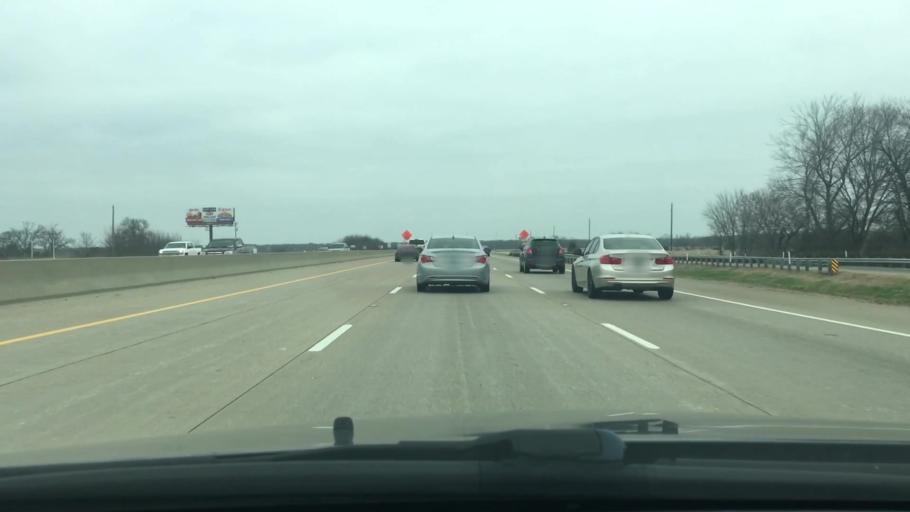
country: US
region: Texas
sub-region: Navarro County
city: Corsicana
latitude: 32.1801
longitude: -96.4715
